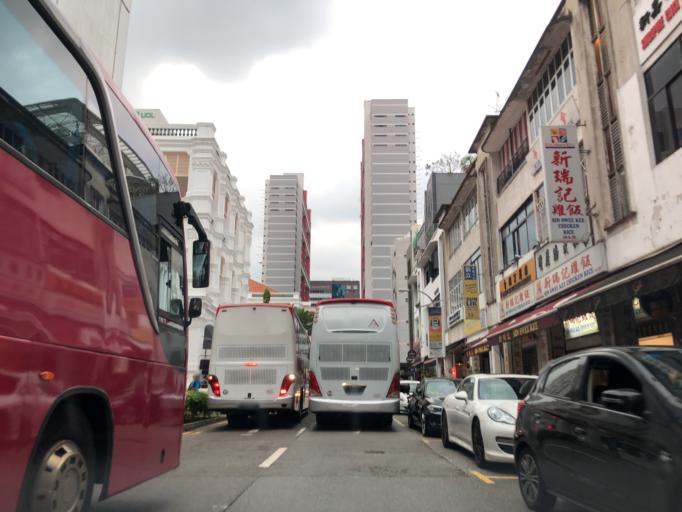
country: SG
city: Singapore
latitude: 1.2957
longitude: 103.8551
